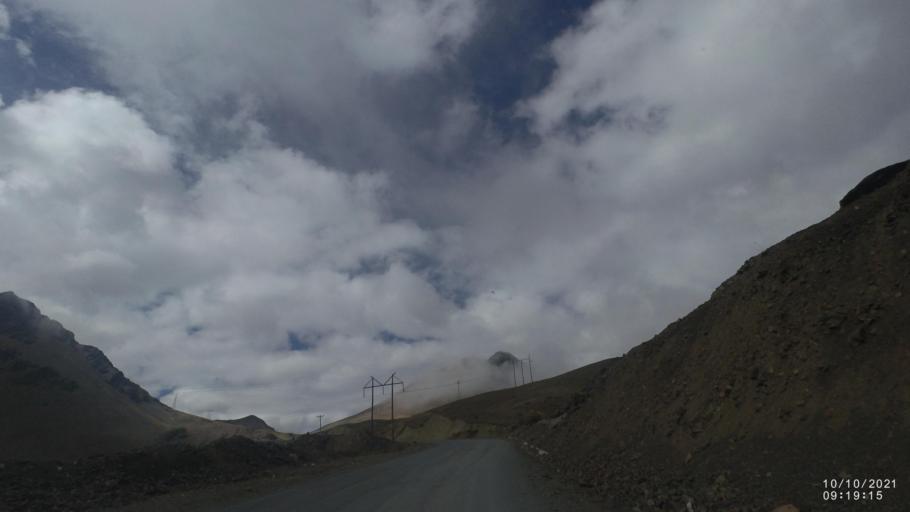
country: BO
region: La Paz
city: Quime
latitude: -17.0524
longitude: -67.2997
